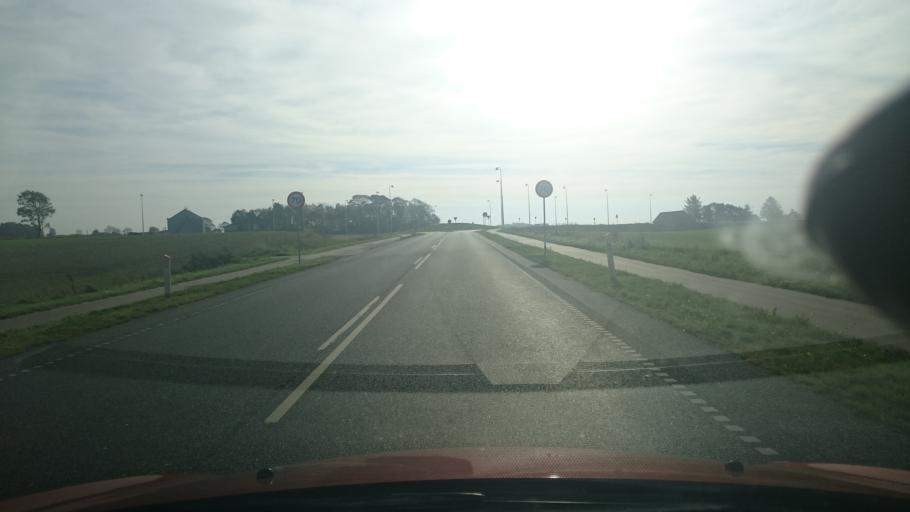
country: DK
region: Central Jutland
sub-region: Syddjurs Kommune
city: Hornslet
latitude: 56.3546
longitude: 10.3447
